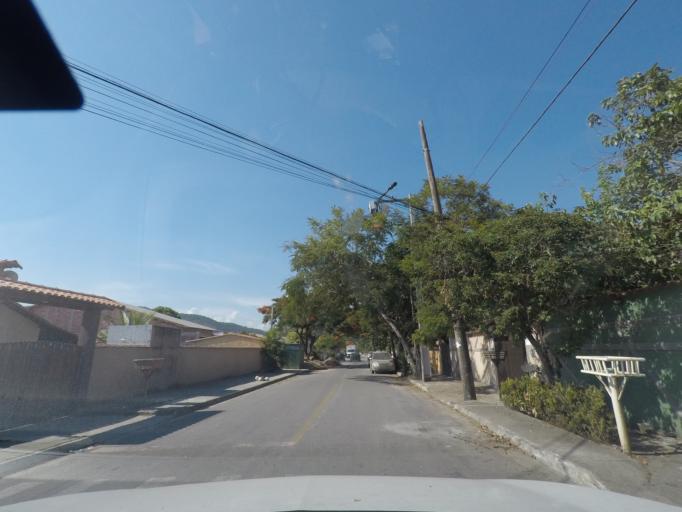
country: BR
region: Rio de Janeiro
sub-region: Niteroi
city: Niteroi
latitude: -22.9647
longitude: -42.9747
